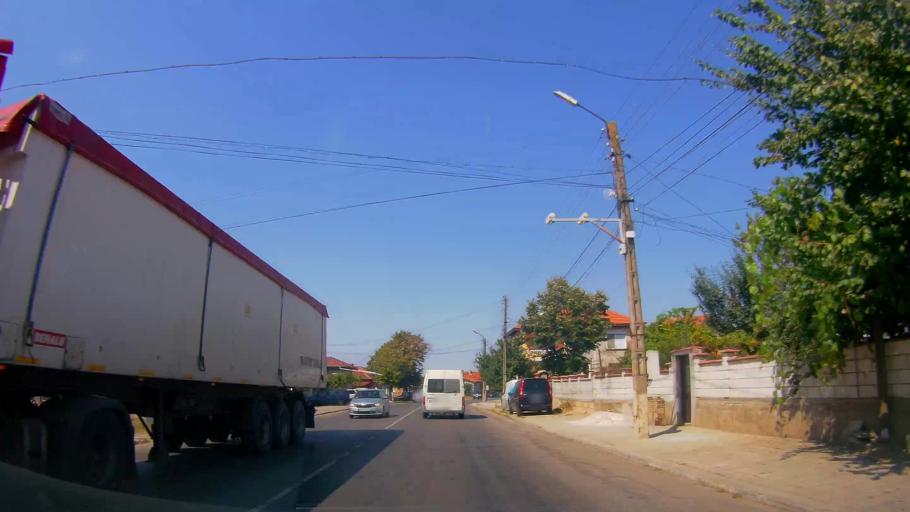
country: BG
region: Razgrad
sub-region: Obshtina Tsar Kaloyan
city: Tsar Kaloyan
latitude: 43.6011
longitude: 26.2453
